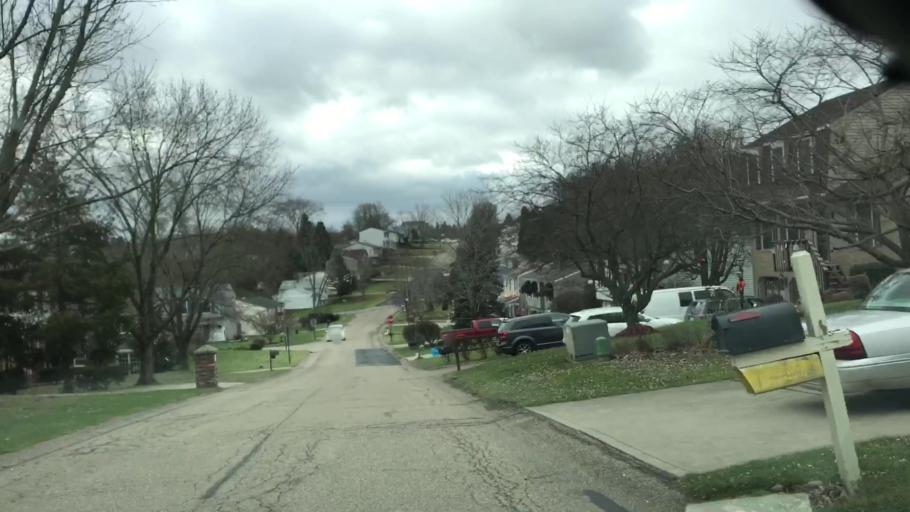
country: US
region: Pennsylvania
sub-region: Allegheny County
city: Enlow
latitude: 40.4489
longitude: -80.2253
